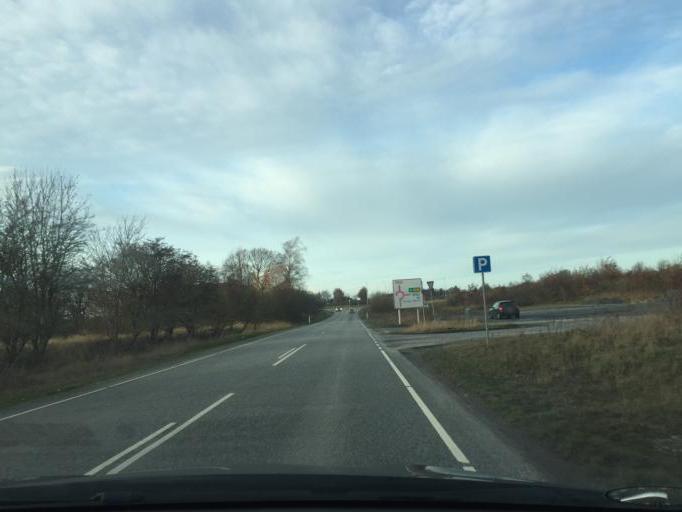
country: DK
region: South Denmark
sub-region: Faaborg-Midtfyn Kommune
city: Ringe
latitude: 55.2546
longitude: 10.4700
